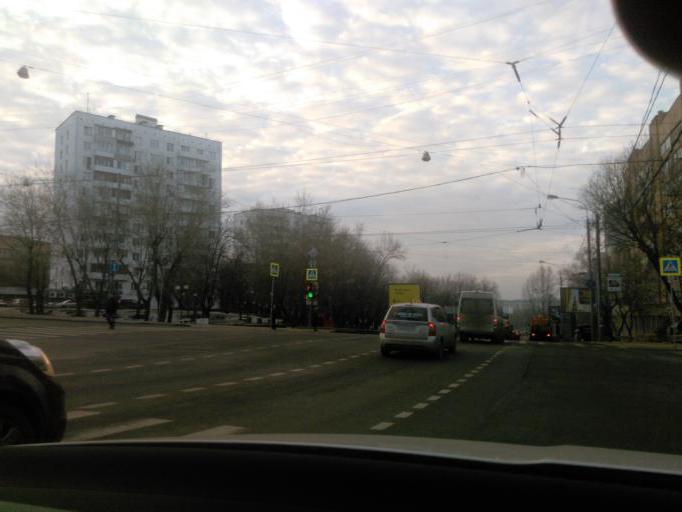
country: RU
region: Moskovskaya
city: Presnenskiy
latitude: 55.7592
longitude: 37.5580
